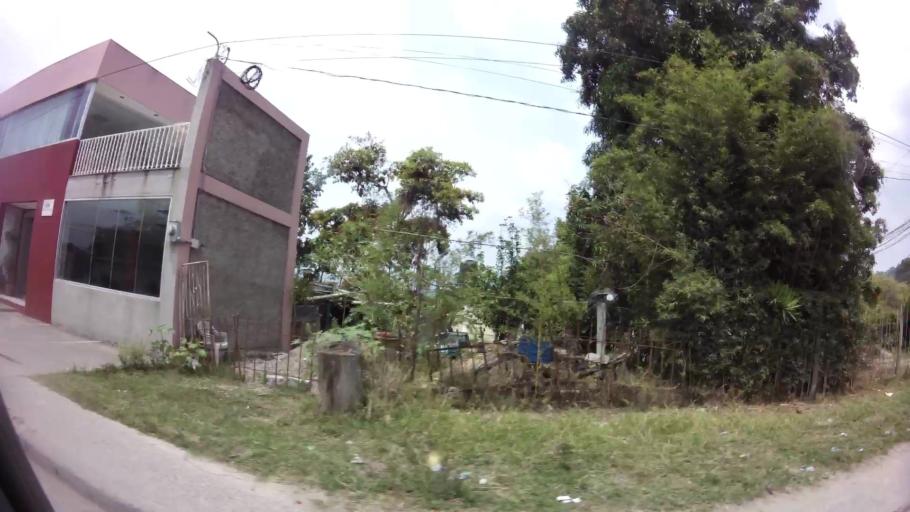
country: HN
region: Comayagua
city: Siguatepeque
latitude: 14.6014
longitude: -87.8374
